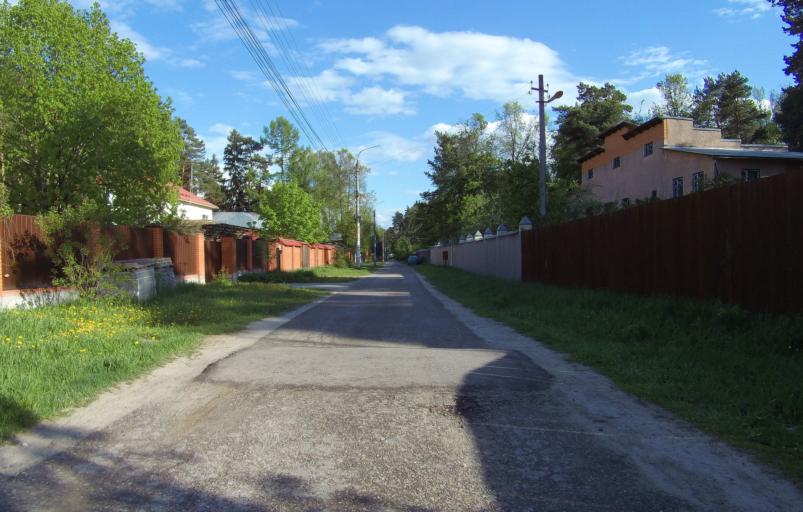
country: RU
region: Moskovskaya
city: Kratovo
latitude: 55.5930
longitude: 38.1675
